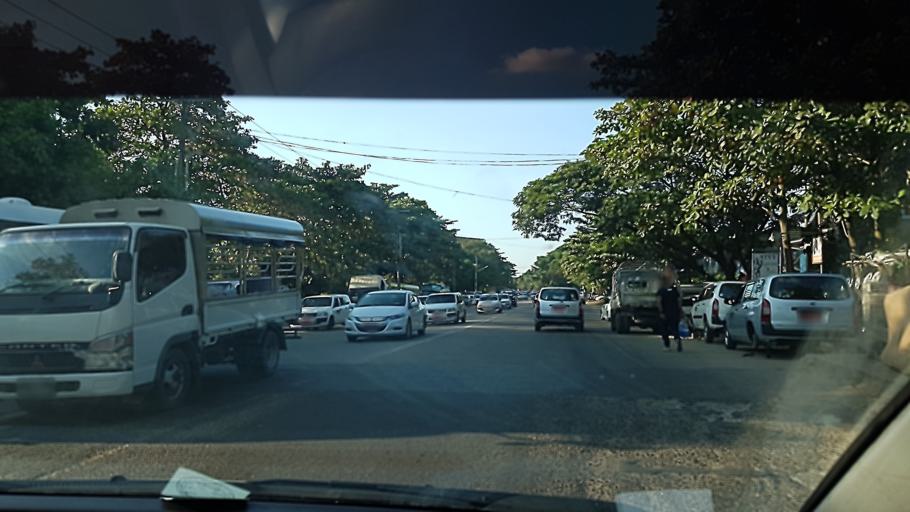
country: MM
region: Yangon
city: Yangon
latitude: 16.8402
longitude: 96.1840
